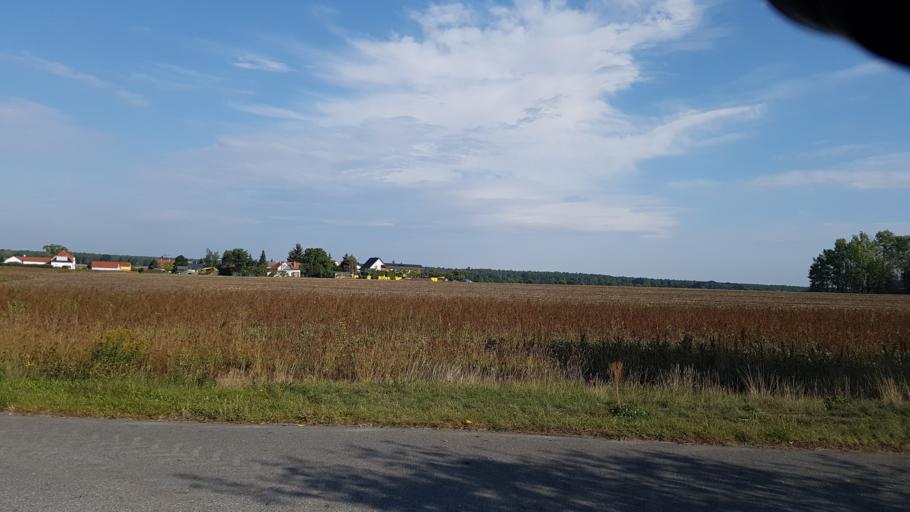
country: DE
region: Brandenburg
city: Plessa
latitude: 51.5294
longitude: 13.6371
